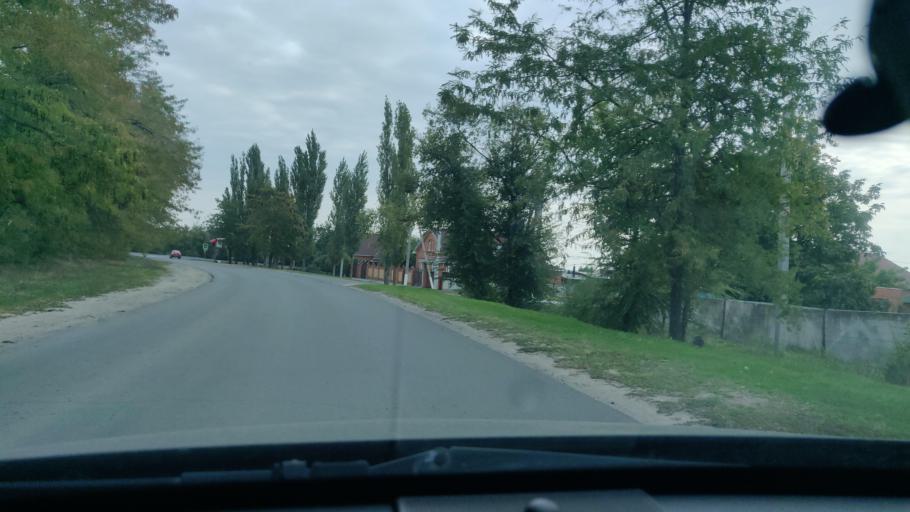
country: RU
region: Rostov
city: Ust'-Donetskiy
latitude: 47.6463
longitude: 40.8712
